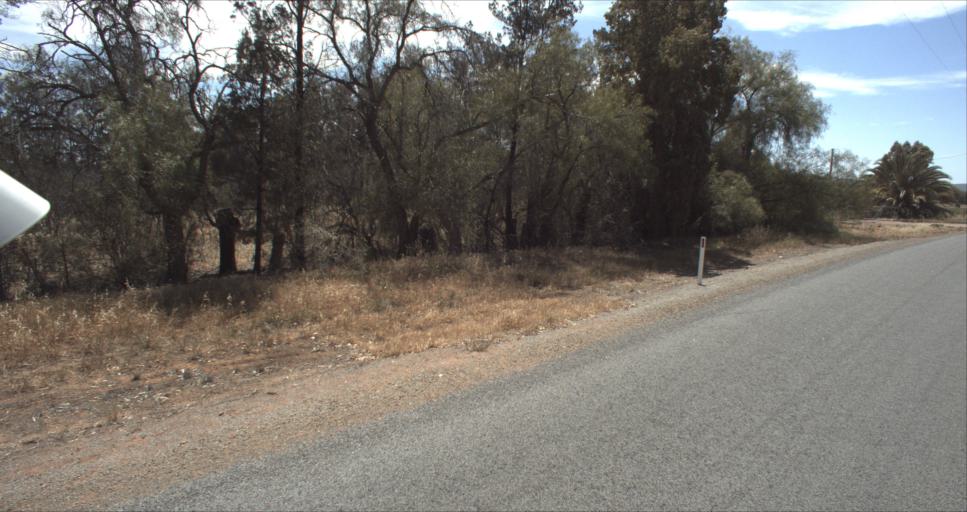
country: AU
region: New South Wales
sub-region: Leeton
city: Leeton
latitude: -34.5726
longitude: 146.4328
